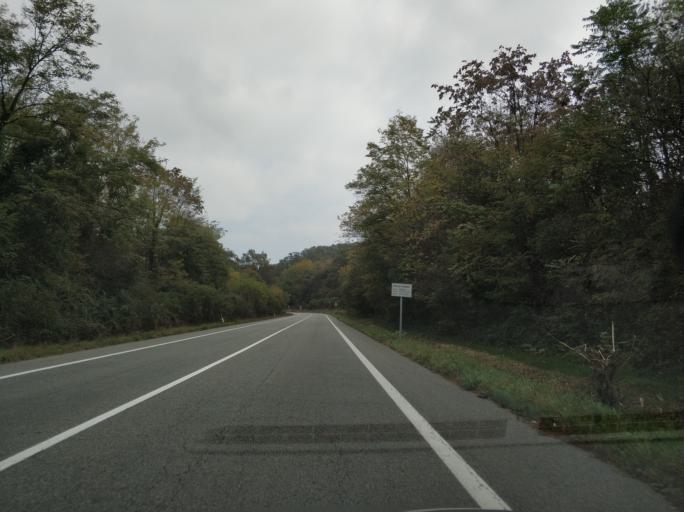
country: IT
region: Piedmont
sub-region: Provincia di Torino
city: Torre Canavese
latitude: 45.3998
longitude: 7.7536
